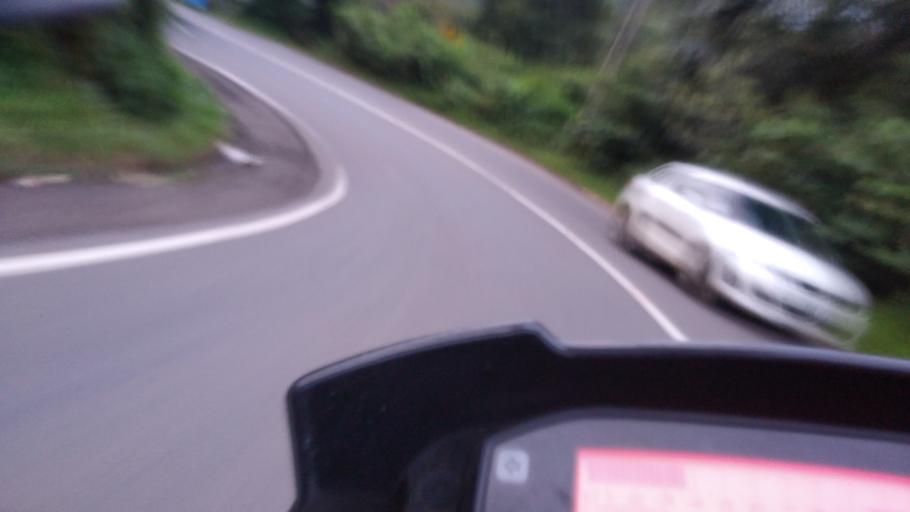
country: IN
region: Kerala
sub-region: Idukki
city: Munnar
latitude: 9.9693
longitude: 77.1246
